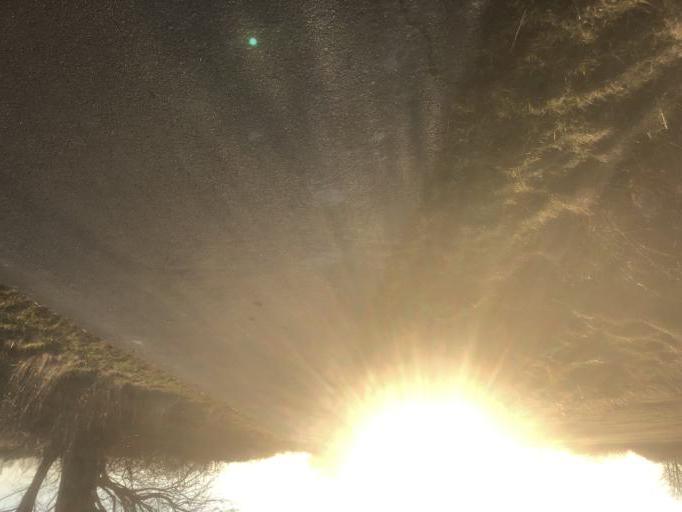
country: DK
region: South Denmark
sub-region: Fredericia Kommune
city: Fredericia
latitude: 55.5874
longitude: 9.7832
